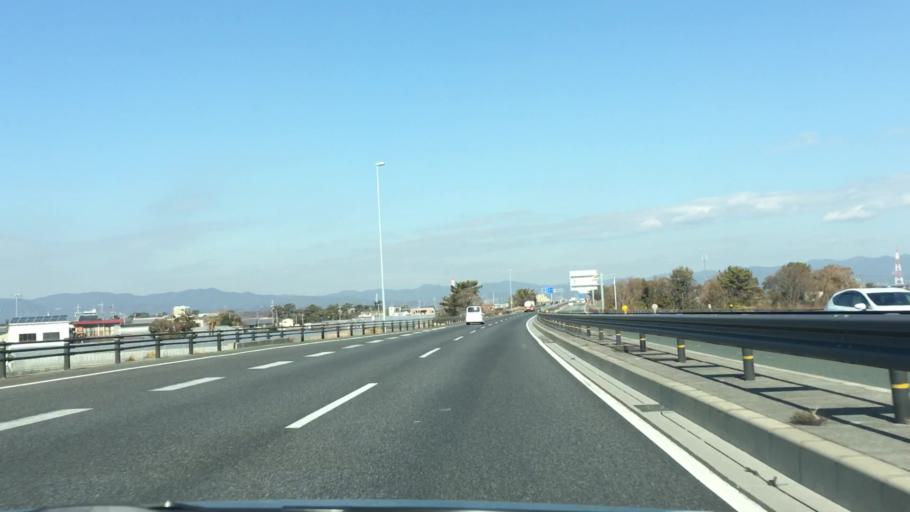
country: JP
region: Aichi
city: Kozakai-cho
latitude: 34.7647
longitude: 137.3322
